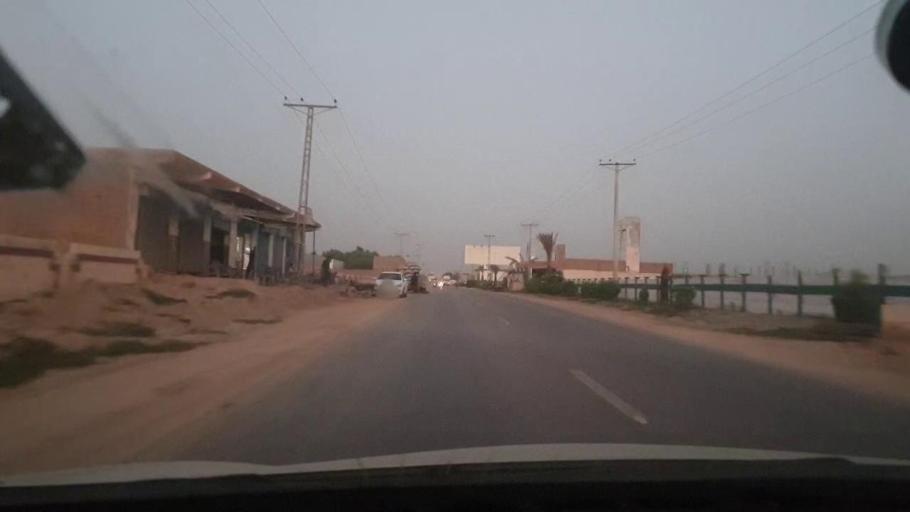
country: PK
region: Sindh
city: Tando Adam
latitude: 25.7476
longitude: 68.6462
